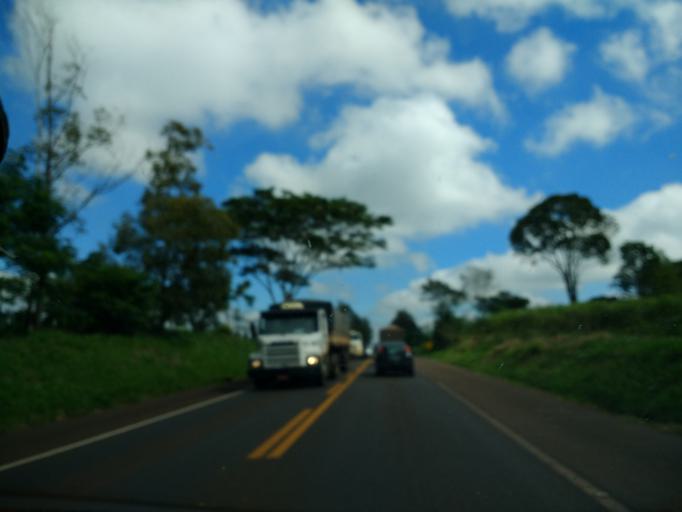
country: BR
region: Parana
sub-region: Cruzeiro Do Oeste
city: Cruzeiro do Oeste
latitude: -23.7678
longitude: -53.1536
